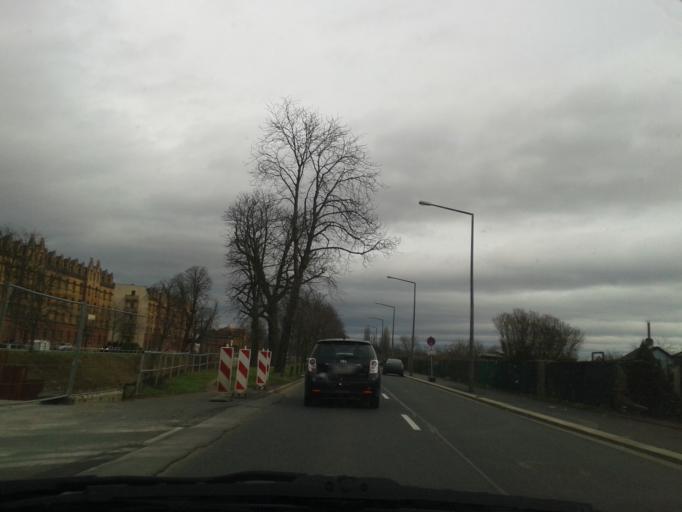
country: DE
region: Saxony
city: Dresden
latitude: 51.0531
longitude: 13.6936
